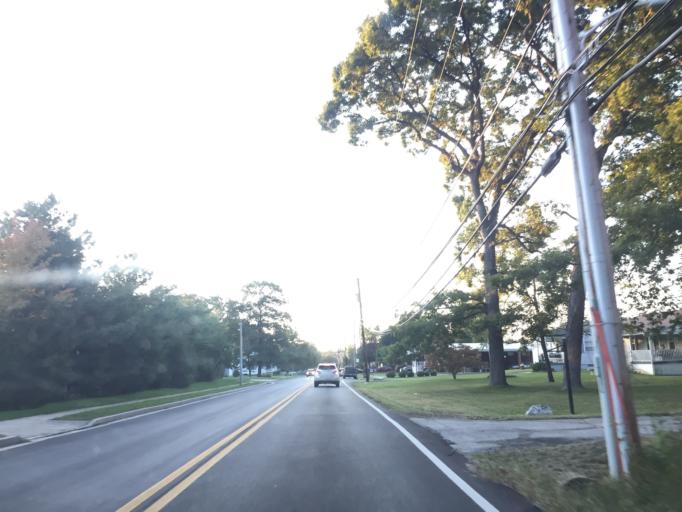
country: US
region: Maryland
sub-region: Baltimore County
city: Essex
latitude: 39.3199
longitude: -76.4692
